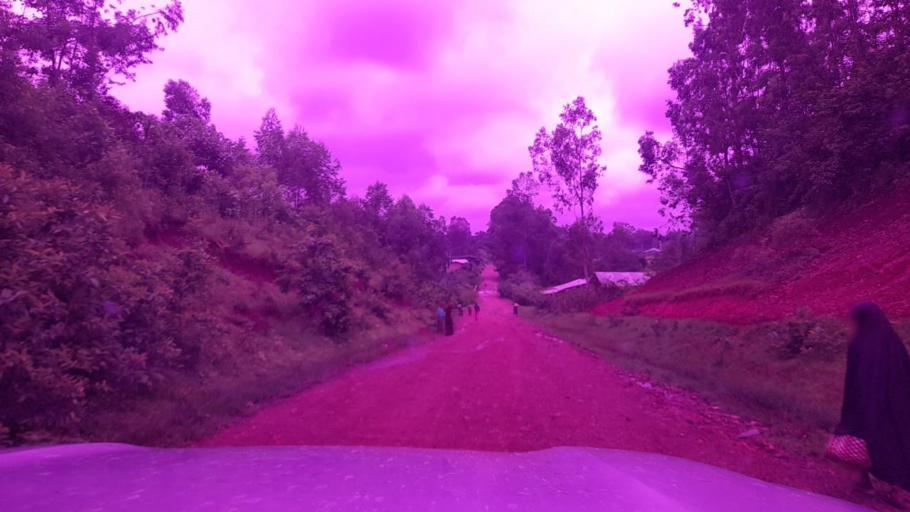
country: ET
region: Southern Nations, Nationalities, and People's Region
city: Bonga
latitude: 7.5744
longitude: 36.0317
